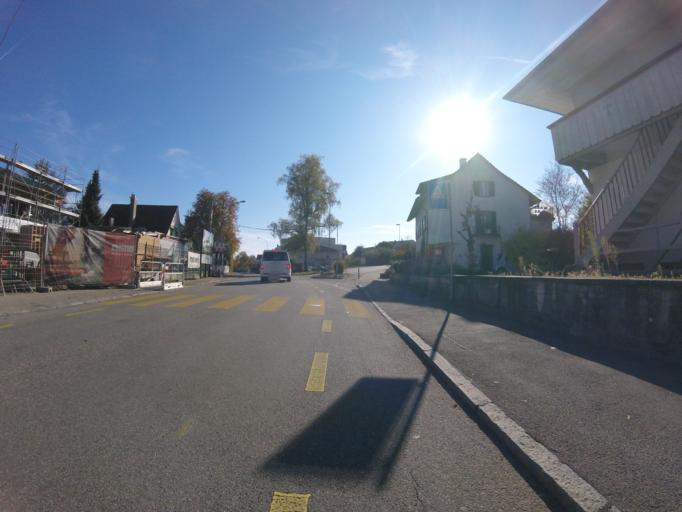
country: CH
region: Bern
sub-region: Bern-Mittelland District
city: Muri
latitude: 46.9328
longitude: 7.4966
